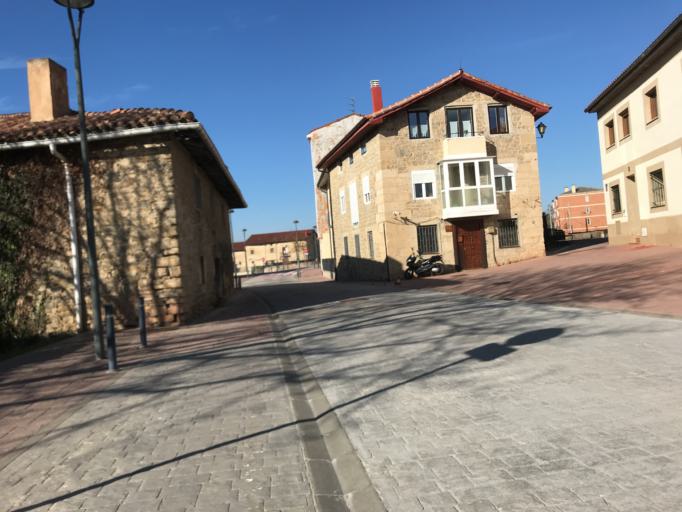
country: ES
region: Basque Country
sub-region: Provincia de Alava
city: Gasteiz / Vitoria
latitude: 42.8301
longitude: -2.6732
